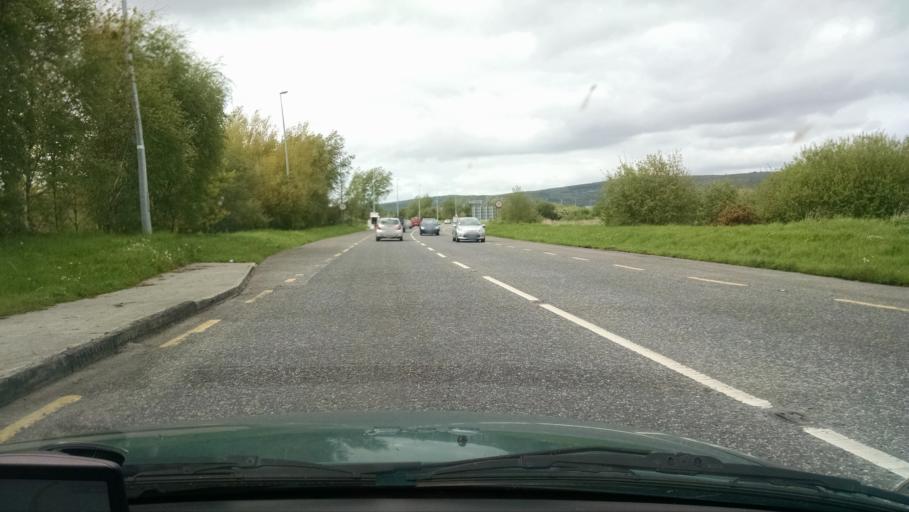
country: IE
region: Munster
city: Moyross
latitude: 52.6659
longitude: -8.6709
